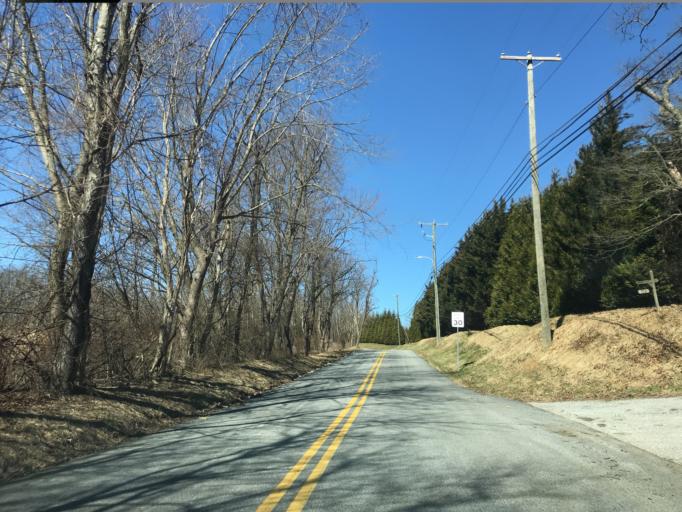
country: US
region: Pennsylvania
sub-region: York County
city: New Freedom
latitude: 39.6814
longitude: -76.6836
